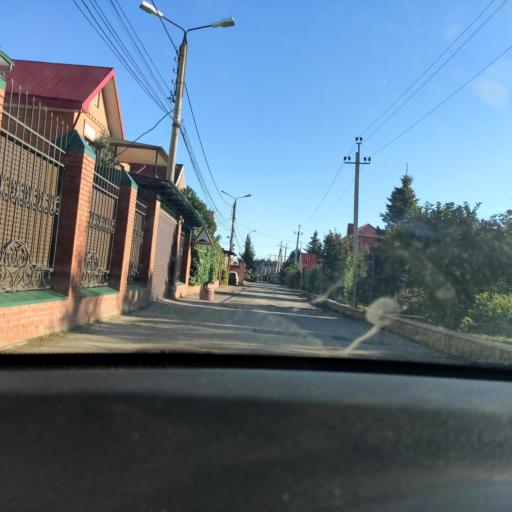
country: RU
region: Samara
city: Samara
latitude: 53.1529
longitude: 50.0824
